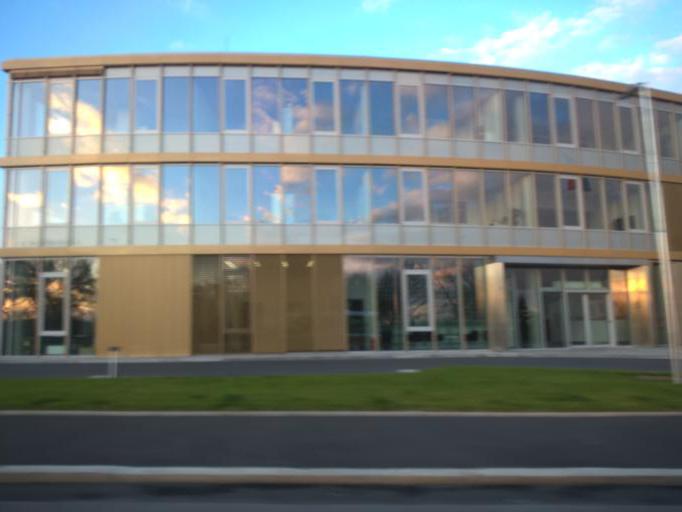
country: CZ
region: Praha
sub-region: Praha 1
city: Mala Strana
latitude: 50.0792
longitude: 14.3813
